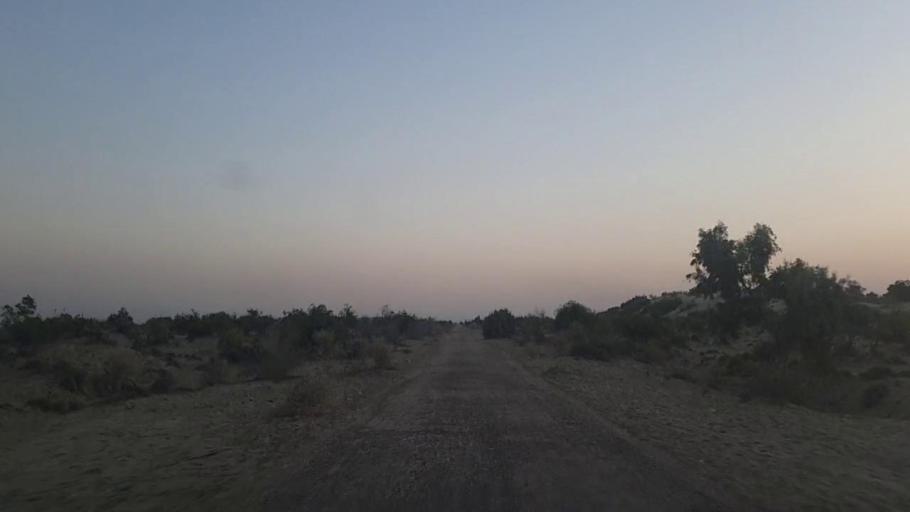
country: PK
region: Sindh
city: Jam Sahib
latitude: 26.4128
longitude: 68.8094
